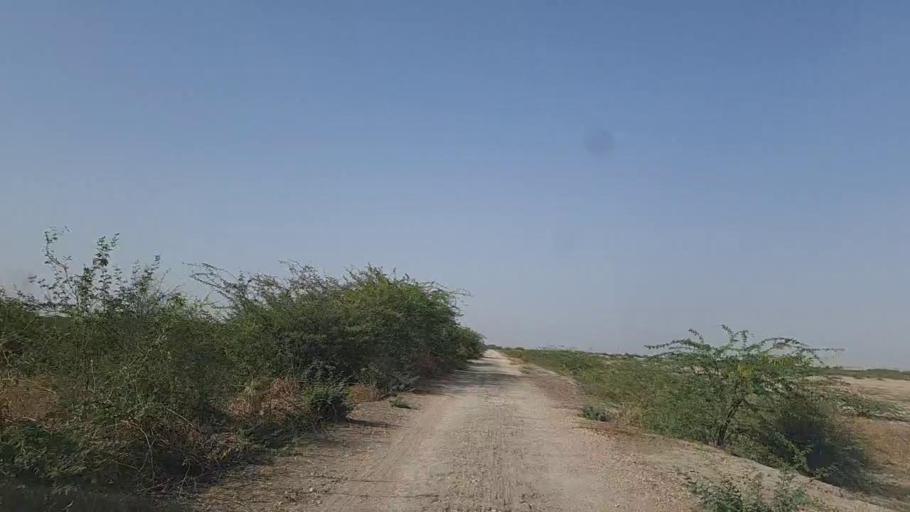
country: PK
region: Sindh
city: Naukot
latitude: 24.6056
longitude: 69.2747
